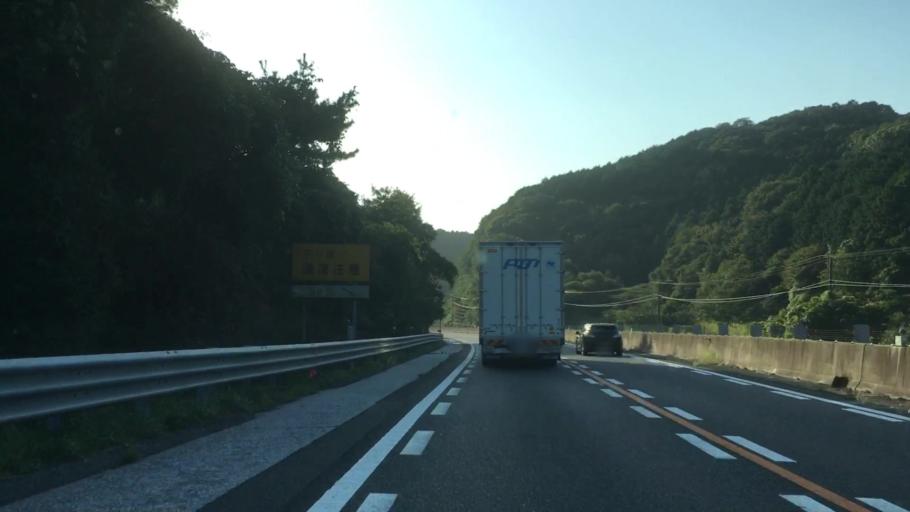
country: JP
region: Yamaguchi
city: Onoda
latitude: 34.1169
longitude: 131.1972
